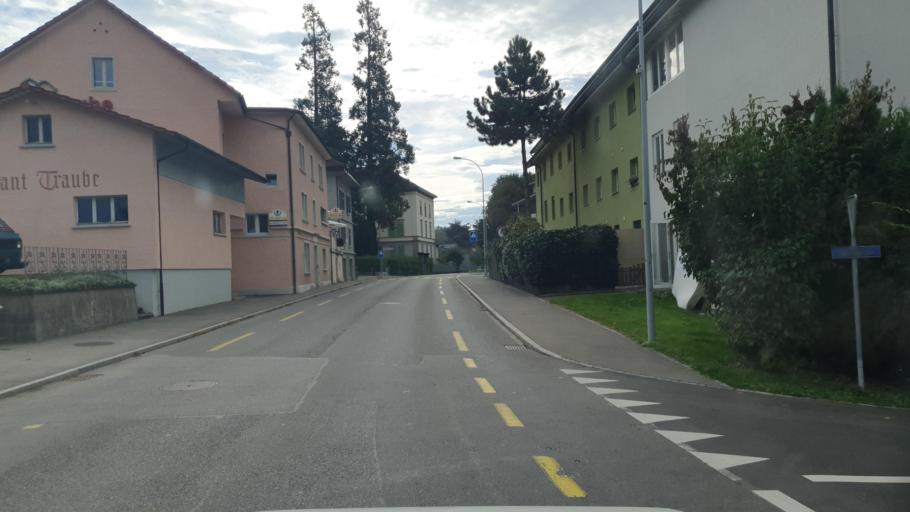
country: CH
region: Aargau
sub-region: Bezirk Lenzburg
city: Meisterschwanden
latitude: 47.2949
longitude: 8.2290
